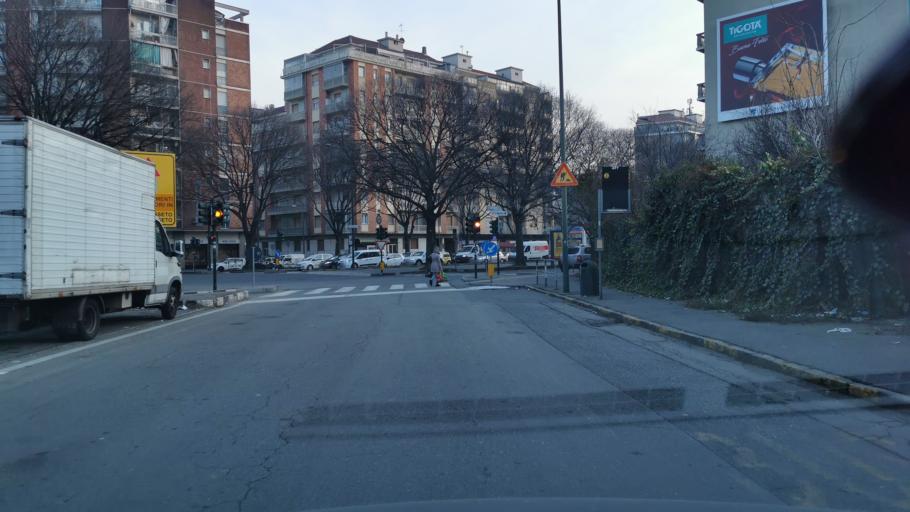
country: IT
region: Piedmont
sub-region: Provincia di Torino
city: Venaria Reale
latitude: 45.0967
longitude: 7.6571
